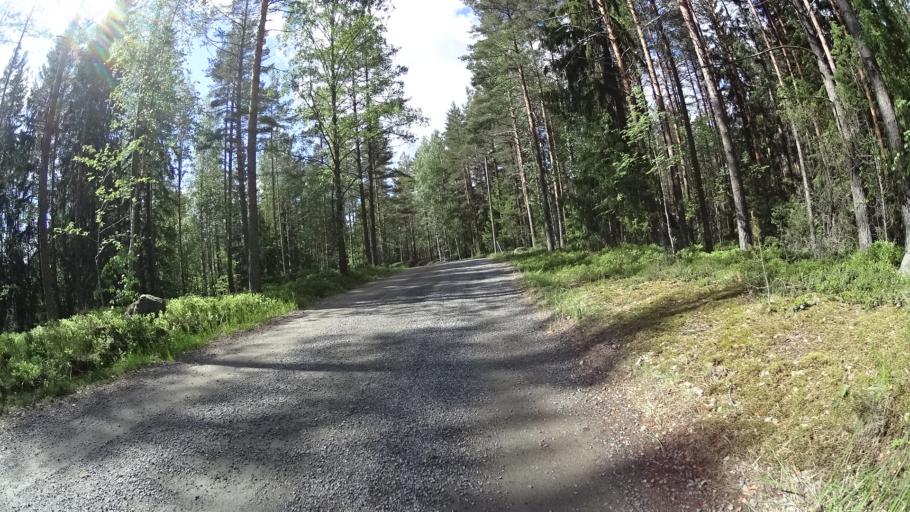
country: FI
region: Uusimaa
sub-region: Raaseporin
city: Pohja
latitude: 60.1858
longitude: 23.5779
